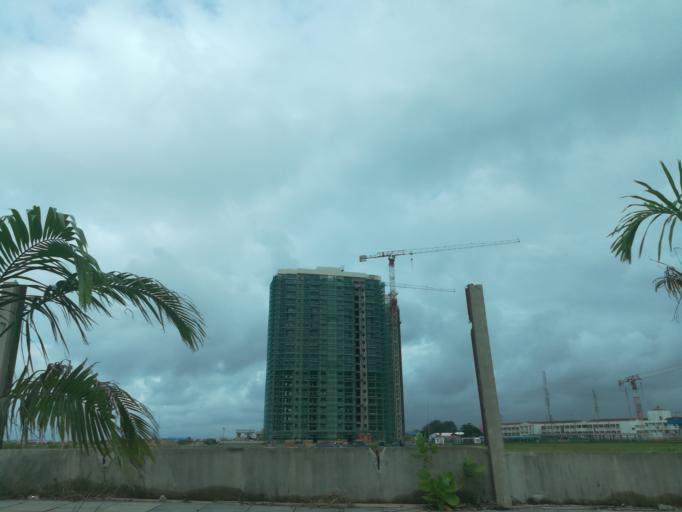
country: NG
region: Lagos
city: Lagos
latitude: 6.4182
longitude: 3.4131
